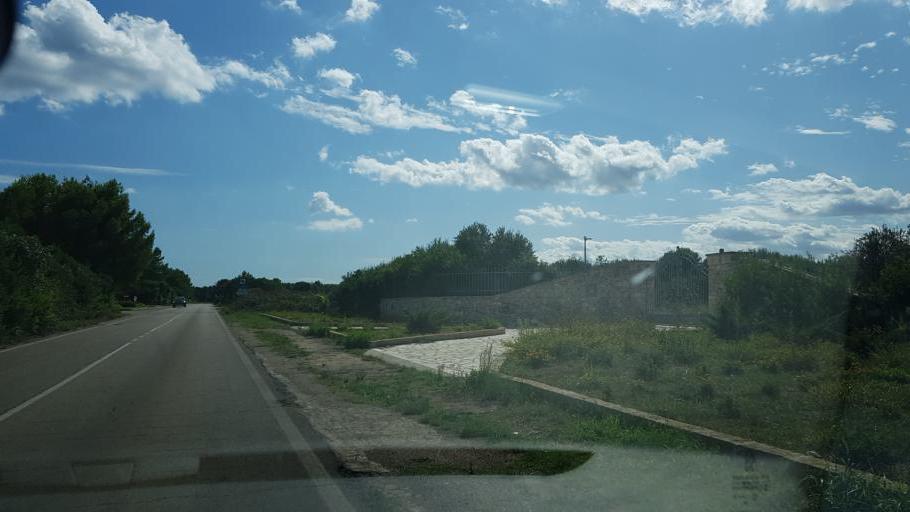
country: IT
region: Apulia
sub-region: Provincia di Lecce
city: Borgagne
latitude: 40.2442
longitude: 18.4425
